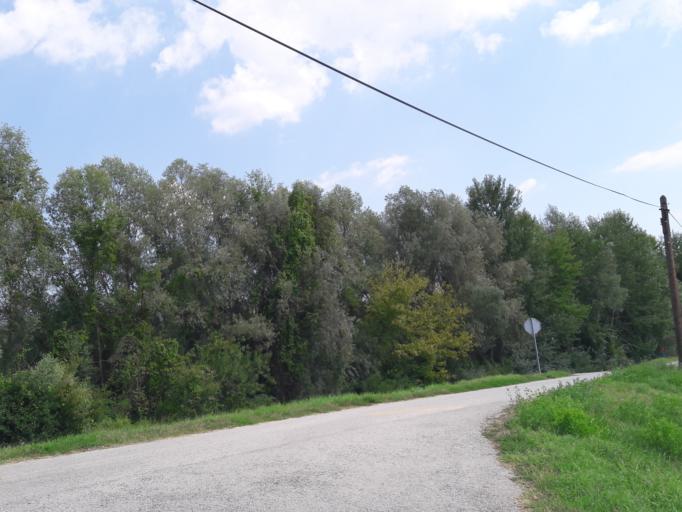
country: HR
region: Osjecko-Baranjska
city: Visnjevac
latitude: 45.5714
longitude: 18.6504
